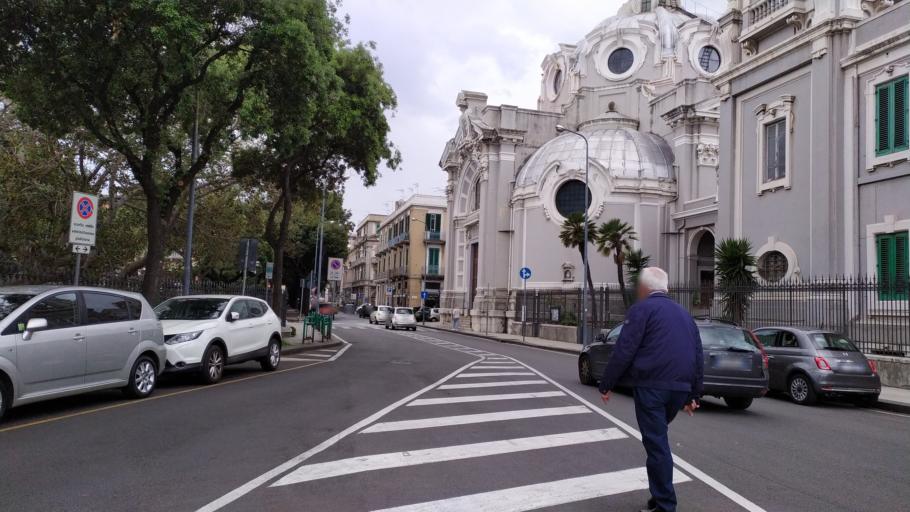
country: IT
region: Sicily
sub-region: Messina
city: Messina
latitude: 38.1887
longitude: 15.5514
